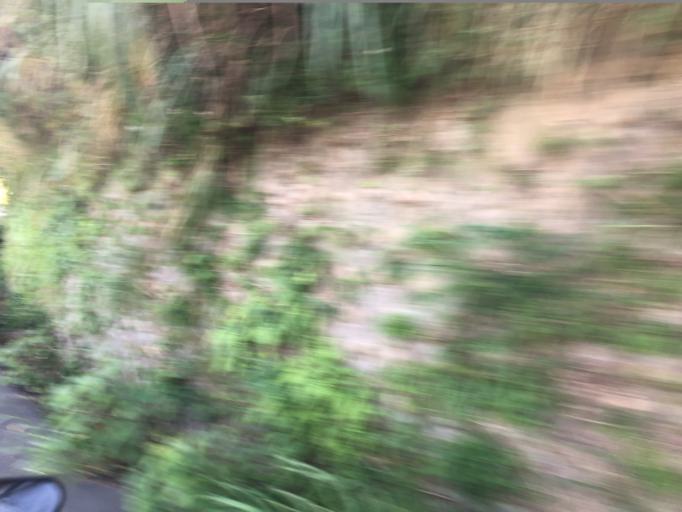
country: TW
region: Taiwan
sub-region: Hsinchu
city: Hsinchu
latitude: 24.7467
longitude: 120.9772
